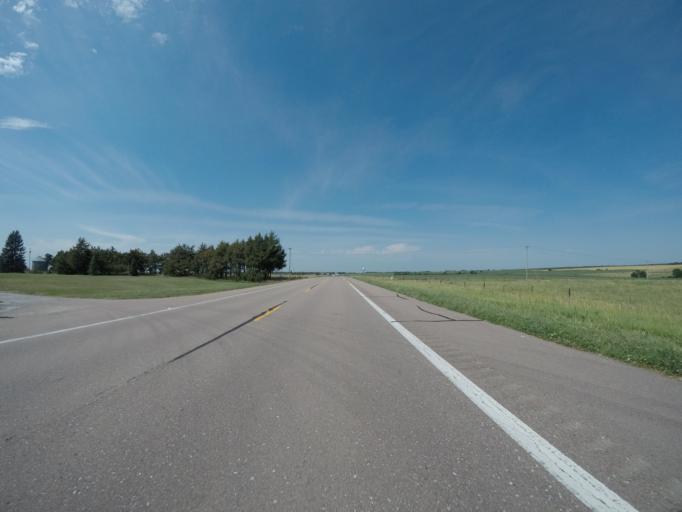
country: US
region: Nebraska
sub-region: Webster County
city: Red Cloud
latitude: 40.3058
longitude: -98.4438
